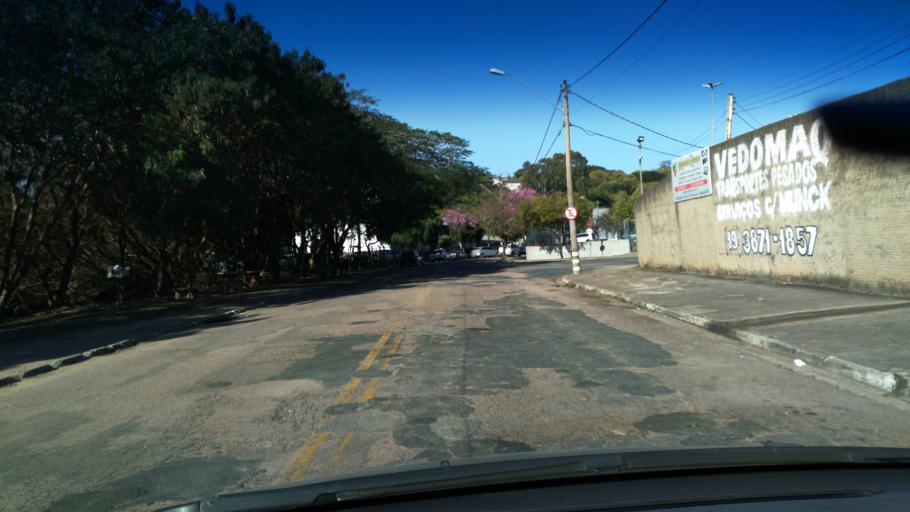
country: BR
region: Sao Paulo
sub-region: Valinhos
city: Valinhos
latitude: -22.9615
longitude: -46.9894
